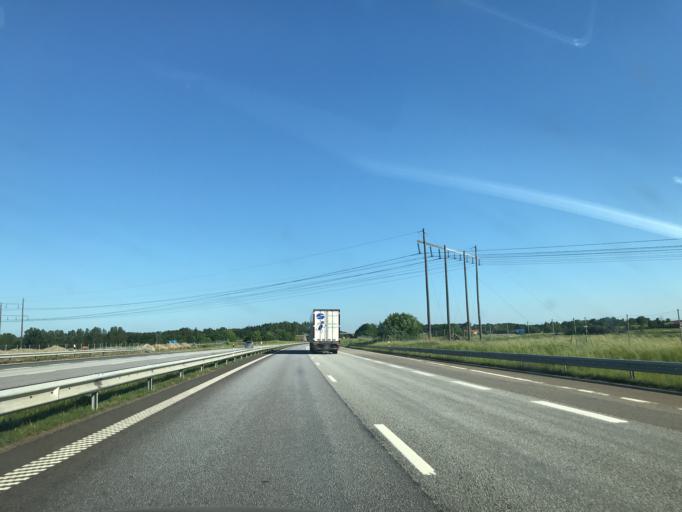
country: SE
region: Halland
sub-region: Varbergs Kommun
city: Traslovslage
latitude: 57.1239
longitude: 12.3168
